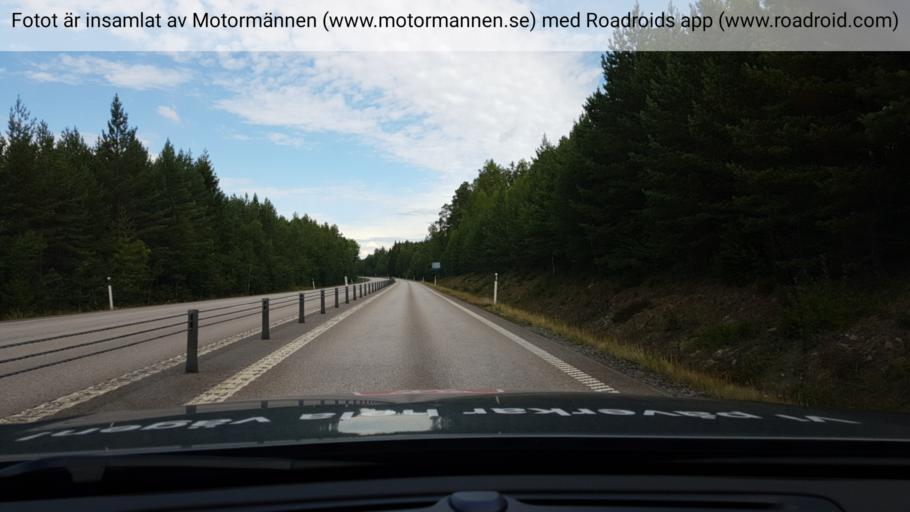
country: SE
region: Uppsala
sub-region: Heby Kommun
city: Tarnsjo
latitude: 60.2791
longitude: 16.9304
